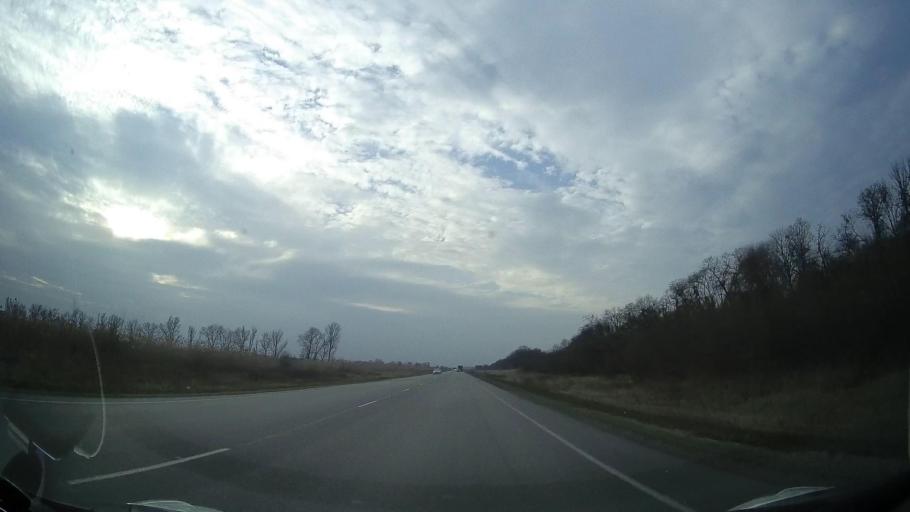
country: RU
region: Rostov
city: Ol'ginskaya
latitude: 47.1311
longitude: 39.9439
